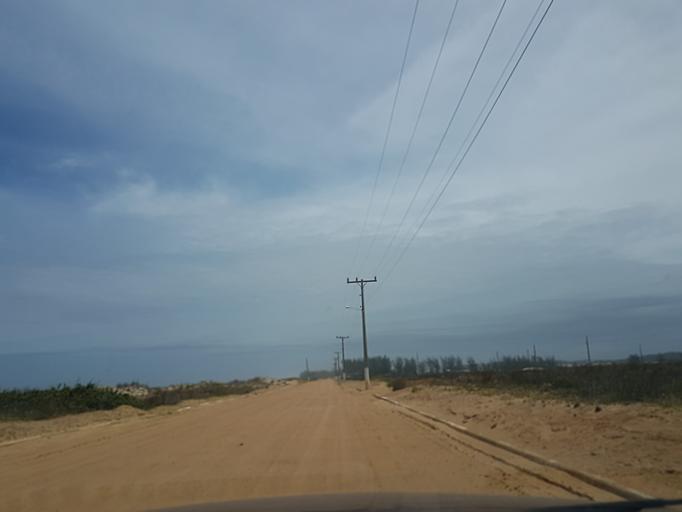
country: BR
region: Santa Catarina
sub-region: Jaguaruna
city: Jaguaruna
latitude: -28.6662
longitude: -48.9662
